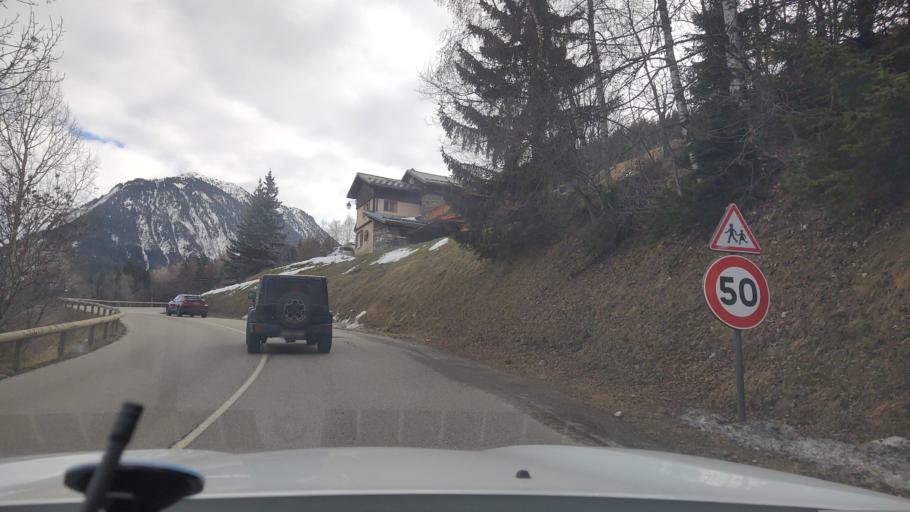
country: FR
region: Rhone-Alpes
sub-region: Departement de la Savoie
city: Saint-Bon-Tarentaise
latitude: 45.4286
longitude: 6.6327
